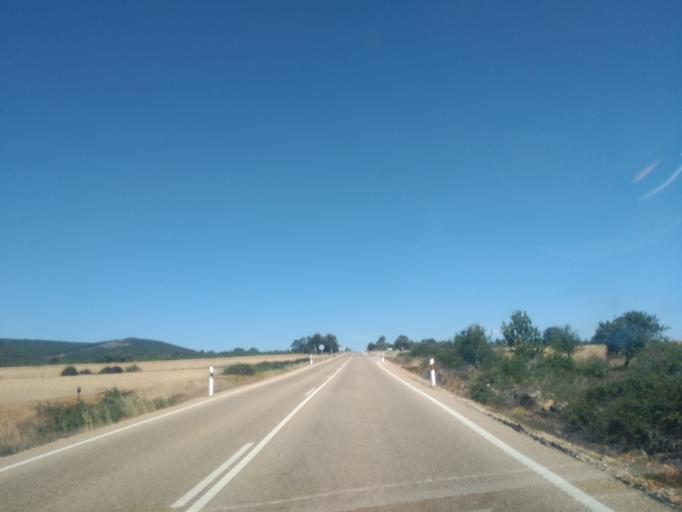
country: ES
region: Castille and Leon
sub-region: Provincia de Zamora
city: Ferreras de Abajo
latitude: 41.9110
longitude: -6.0794
